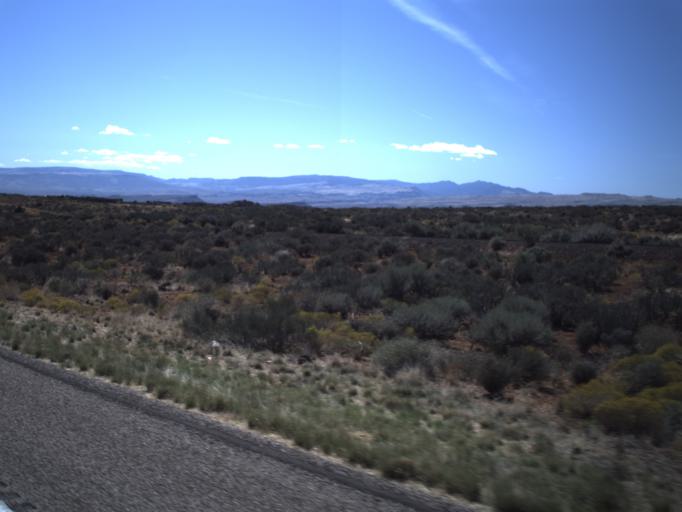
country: US
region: Utah
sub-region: Washington County
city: Ivins
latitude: 37.2139
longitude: -113.6318
